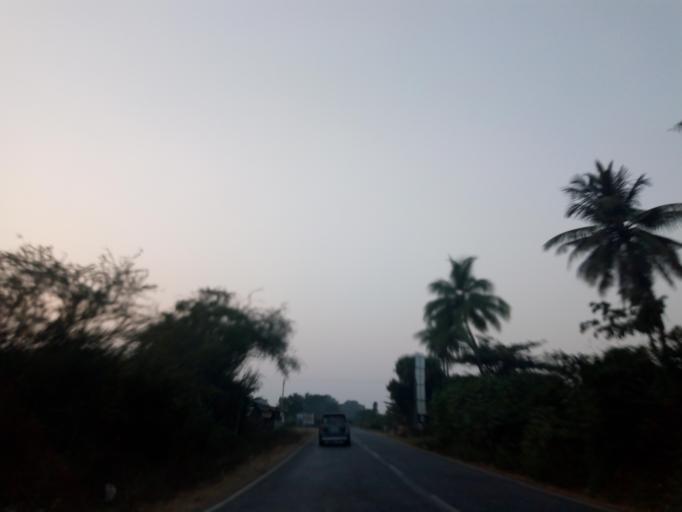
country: IN
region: Andhra Pradesh
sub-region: West Godavari
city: Tadepallegudem
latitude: 16.8182
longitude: 81.4897
